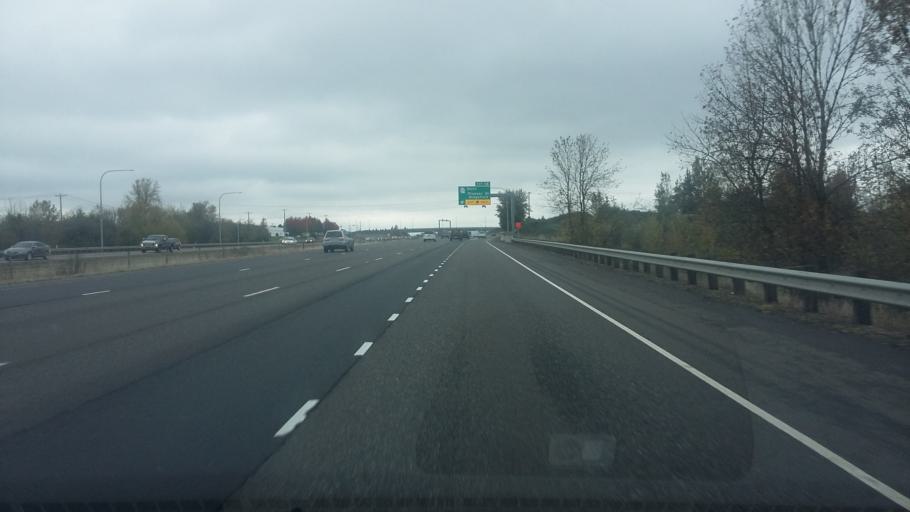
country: US
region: Washington
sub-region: Clark County
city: La Center
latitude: 45.8097
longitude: -122.6828
